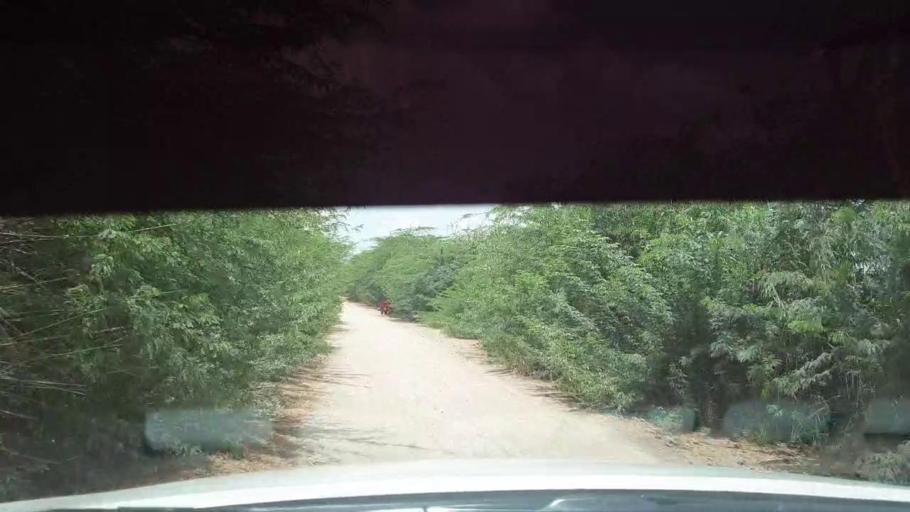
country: PK
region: Sindh
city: Kadhan
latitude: 24.4740
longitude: 68.9915
